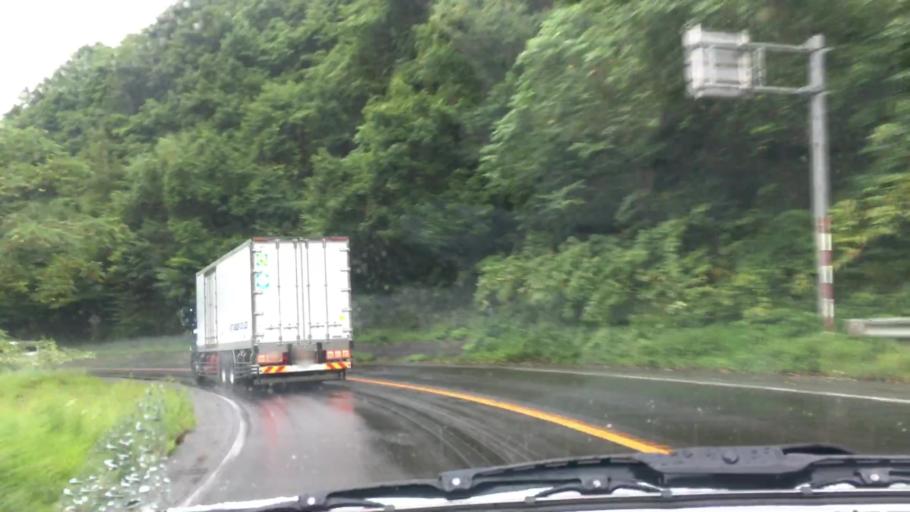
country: JP
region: Hokkaido
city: Niseko Town
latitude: 42.5948
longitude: 140.5929
